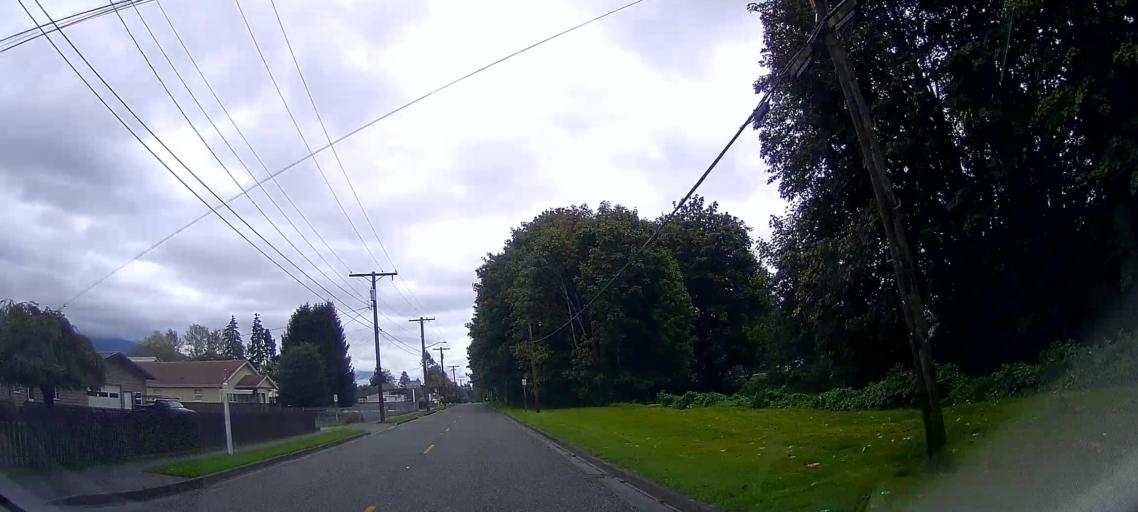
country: US
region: Washington
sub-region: Skagit County
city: Sedro-Woolley
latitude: 48.5263
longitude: -122.0631
